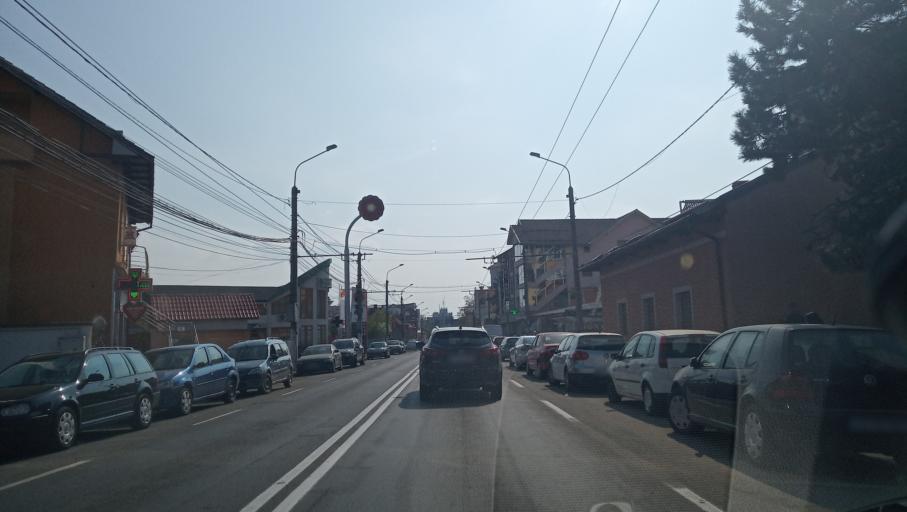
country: RO
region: Gorj
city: Targu Jiu
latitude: 45.0466
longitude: 23.2775
